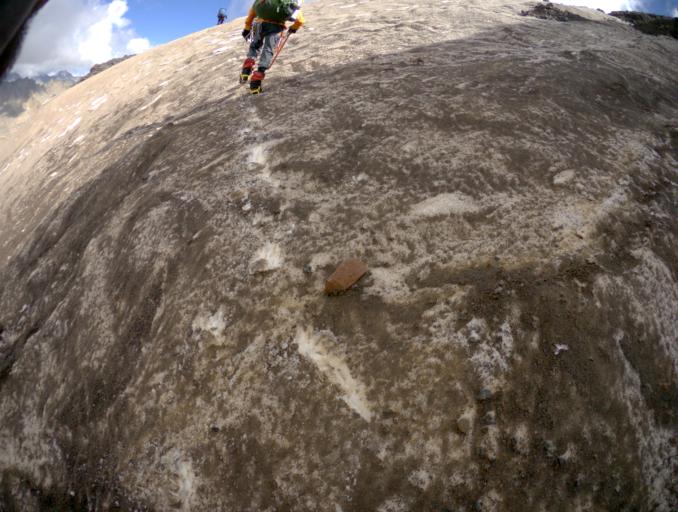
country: RU
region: Kabardino-Balkariya
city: Terskol
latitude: 43.3202
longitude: 42.5100
